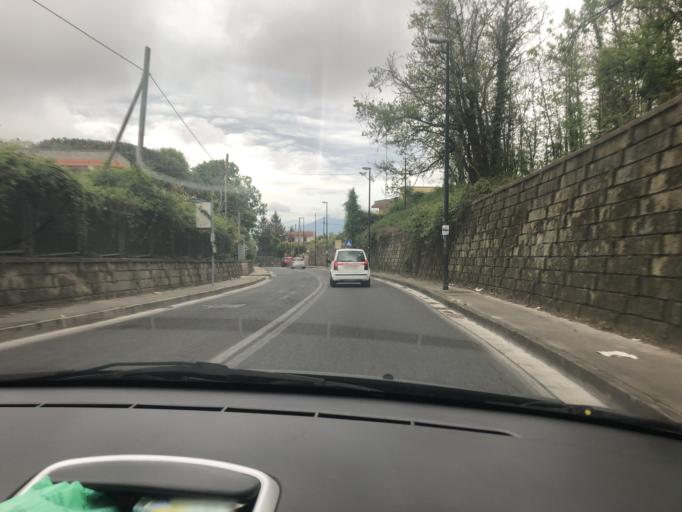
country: IT
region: Campania
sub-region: Provincia di Napoli
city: Torre Caracciolo
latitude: 40.8631
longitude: 14.2042
